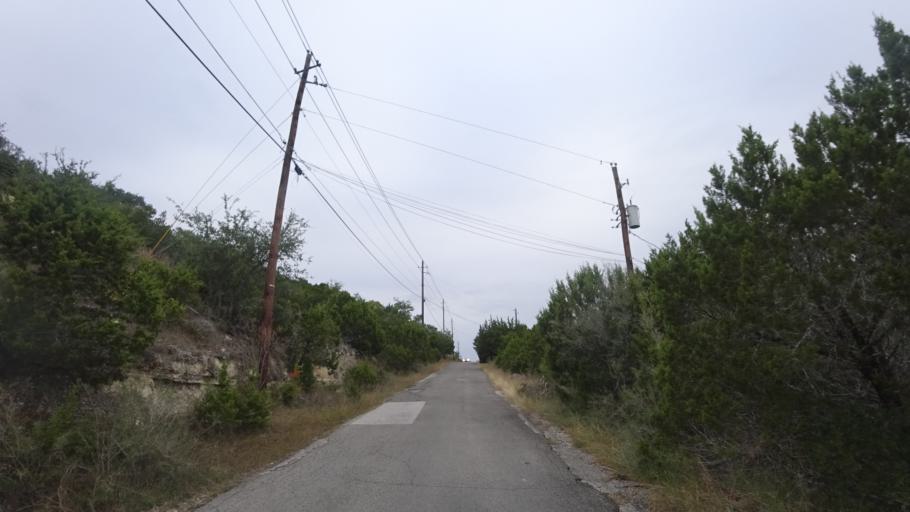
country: US
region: Texas
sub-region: Travis County
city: Hudson Bend
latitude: 30.3728
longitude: -97.9161
